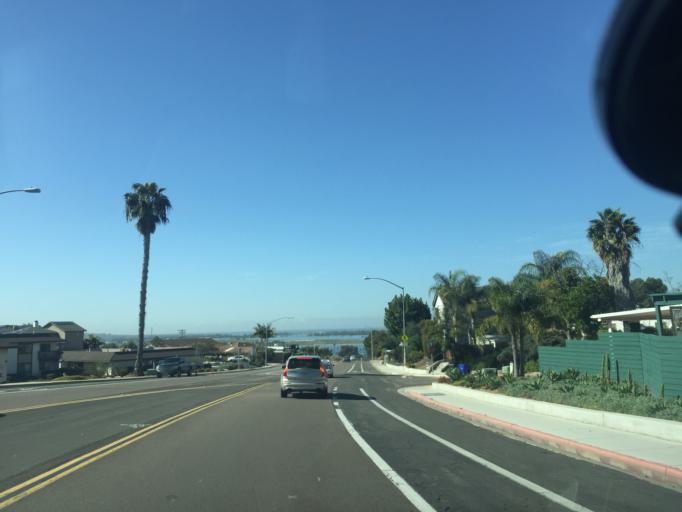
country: US
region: California
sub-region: San Diego County
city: San Diego
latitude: 32.7917
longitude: -117.1974
